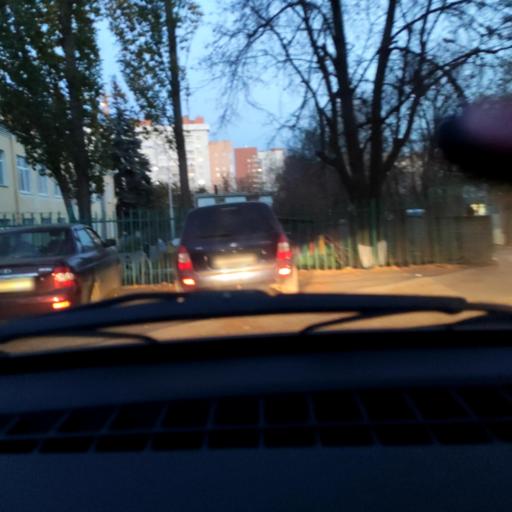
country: RU
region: Bashkortostan
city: Ufa
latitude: 54.7518
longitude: 56.0030
